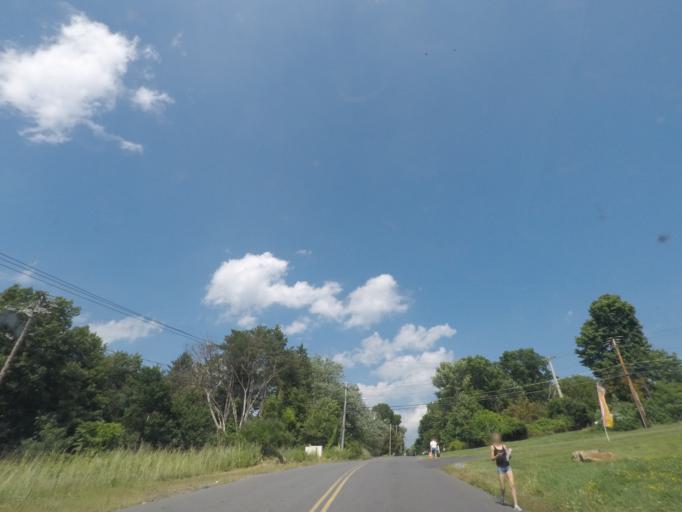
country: US
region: New York
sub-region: Saratoga County
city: Waterford
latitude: 42.7745
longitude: -73.6673
